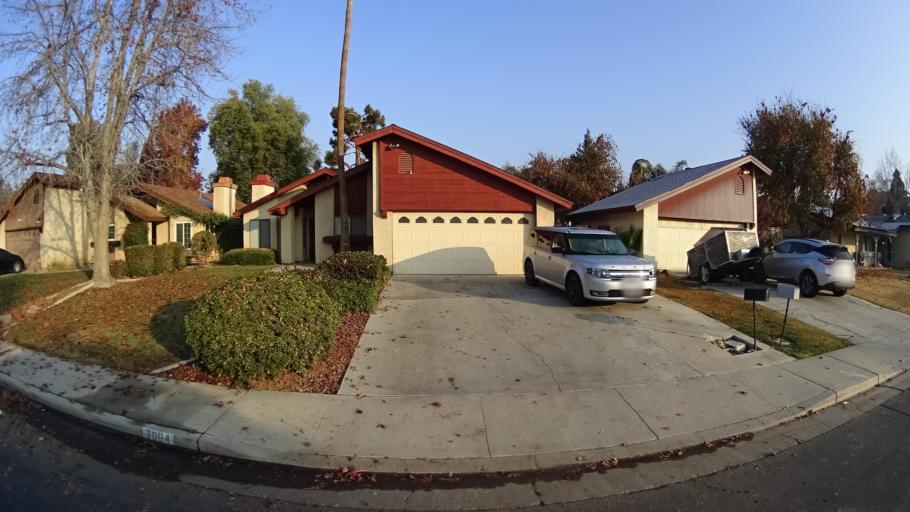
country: US
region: California
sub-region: Kern County
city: Greenacres
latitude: 35.3188
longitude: -119.0822
